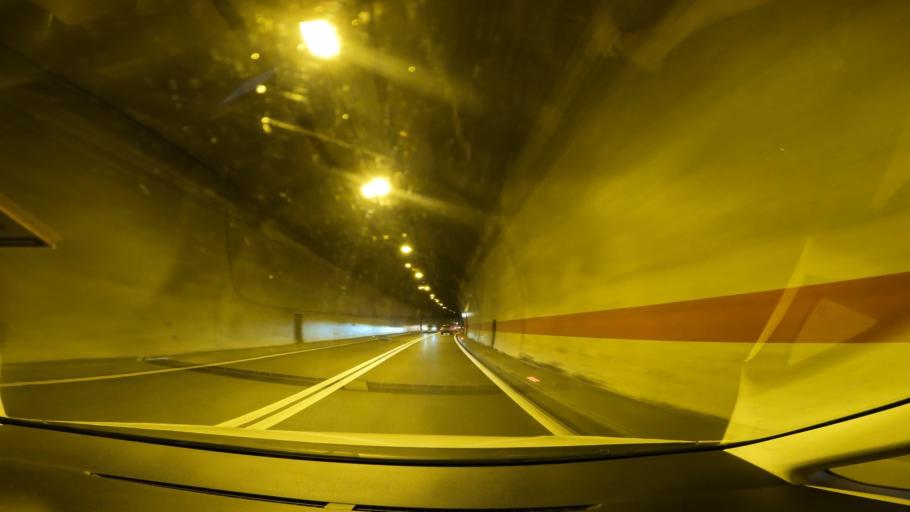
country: HR
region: Krapinsko-Zagorska
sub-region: Grad Krapina
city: Krapina
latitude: 46.1781
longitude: 15.8524
